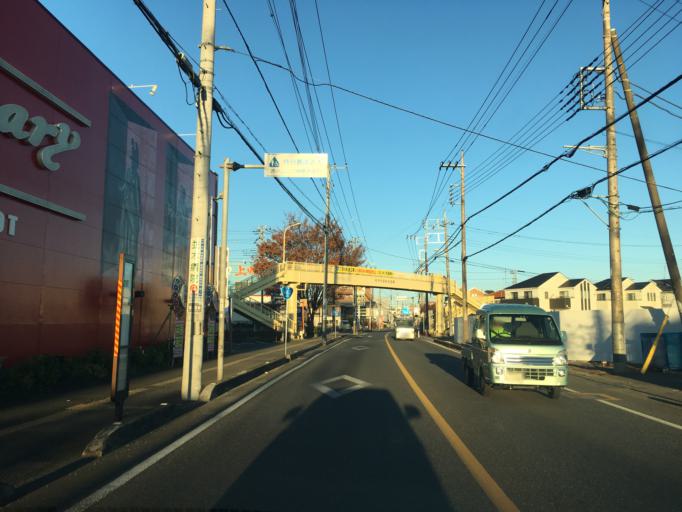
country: JP
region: Saitama
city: Sayama
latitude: 35.8138
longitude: 139.4244
